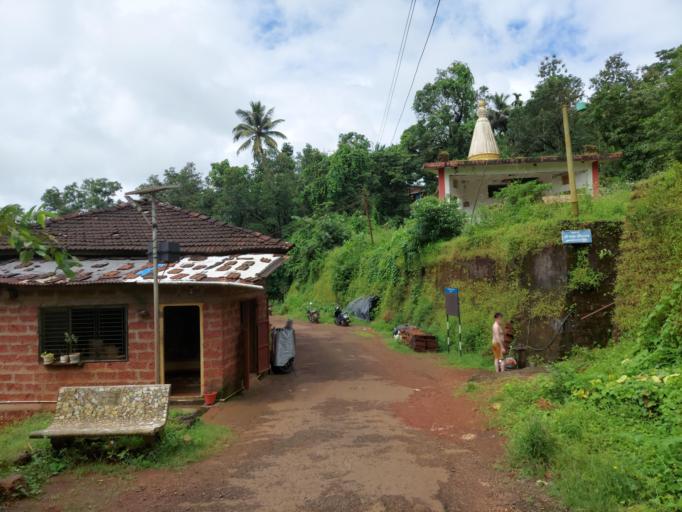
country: IN
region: Maharashtra
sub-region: Ratnagiri
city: Chiplun
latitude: 17.5563
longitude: 73.5068
